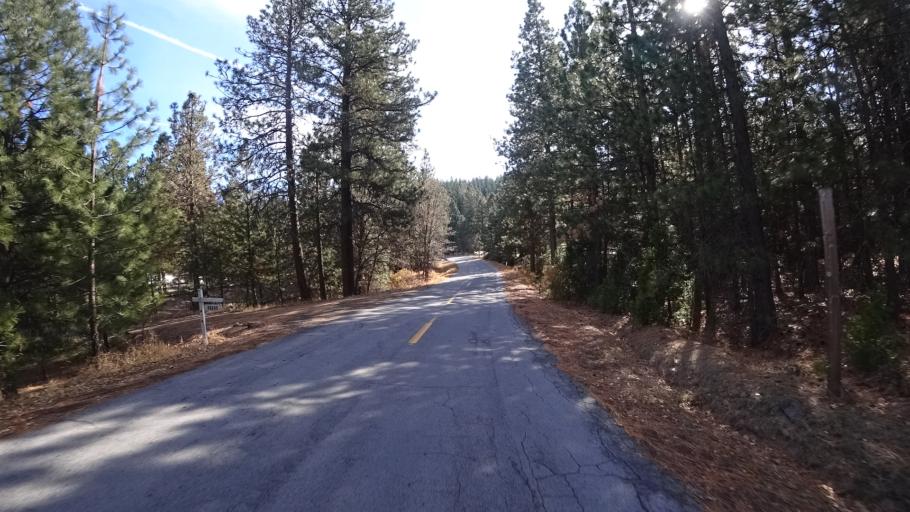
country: US
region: California
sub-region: Siskiyou County
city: Weed
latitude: 41.4320
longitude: -122.4143
